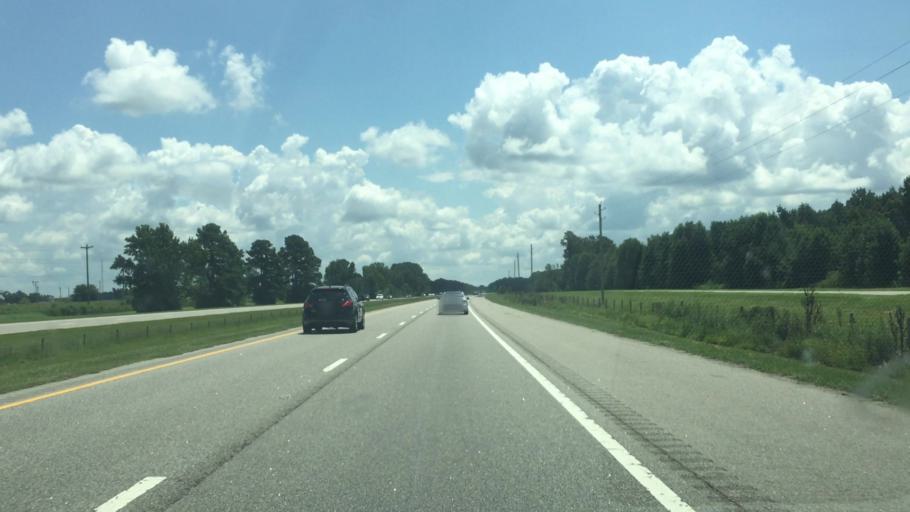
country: US
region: North Carolina
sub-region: Robeson County
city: Lumberton
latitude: 34.5863
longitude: -79.0607
